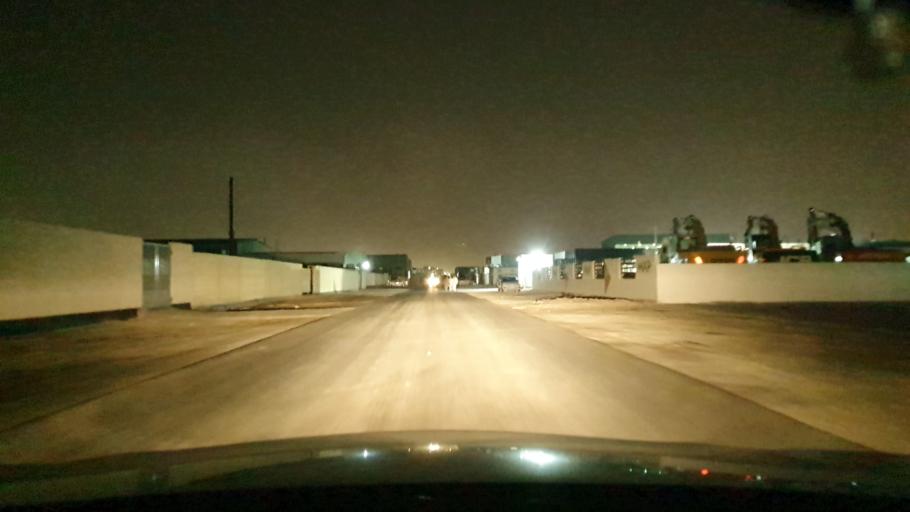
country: BH
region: Northern
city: Sitrah
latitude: 26.0973
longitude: 50.6236
